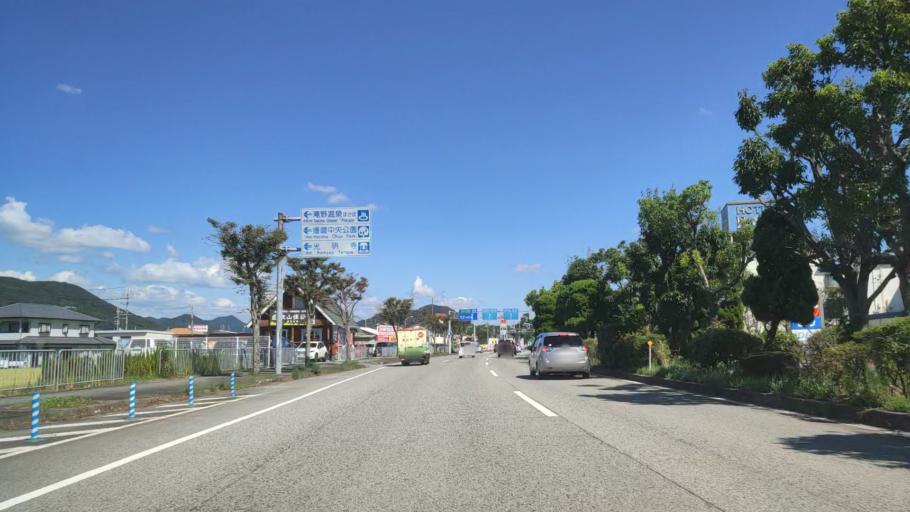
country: JP
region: Hyogo
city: Yashiro
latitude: 34.9308
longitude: 134.9596
